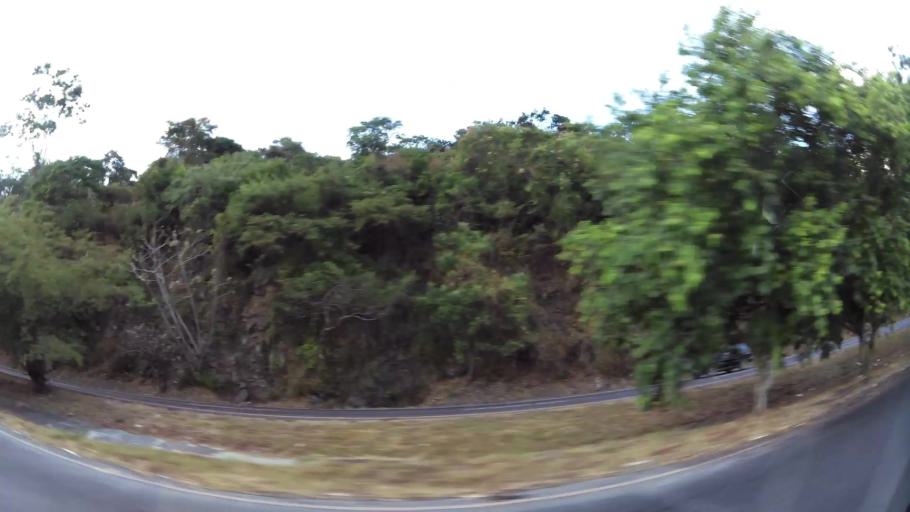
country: SV
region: San Vicente
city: Apastepeque
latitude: 13.6658
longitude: -88.8214
